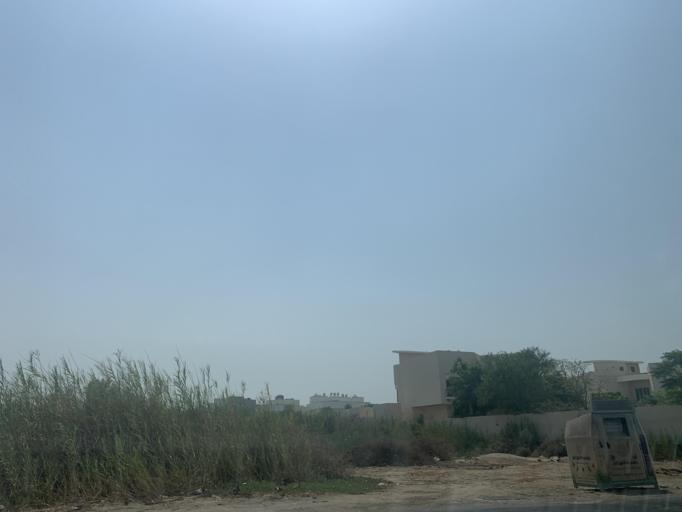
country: BH
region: Northern
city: Madinat `Isa
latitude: 26.1961
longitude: 50.4957
